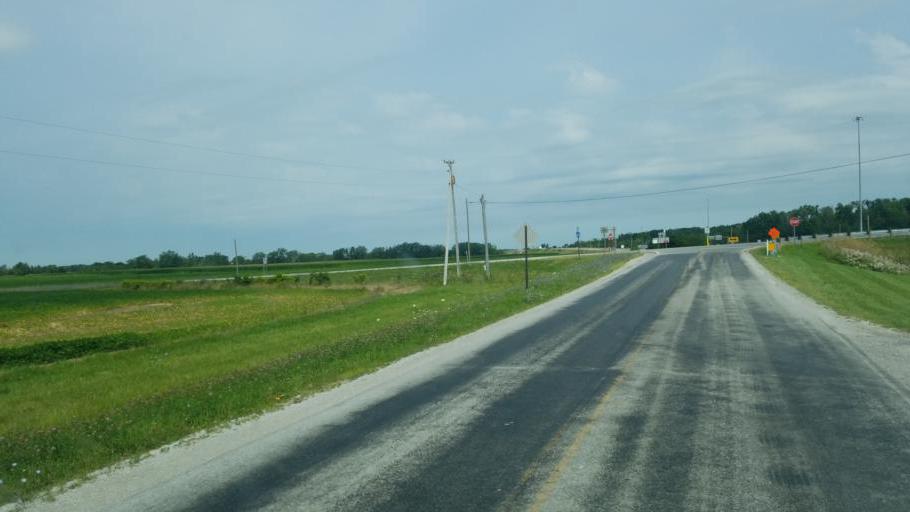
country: US
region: Ohio
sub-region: Wyandot County
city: Carey
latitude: 40.9388
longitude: -83.4021
